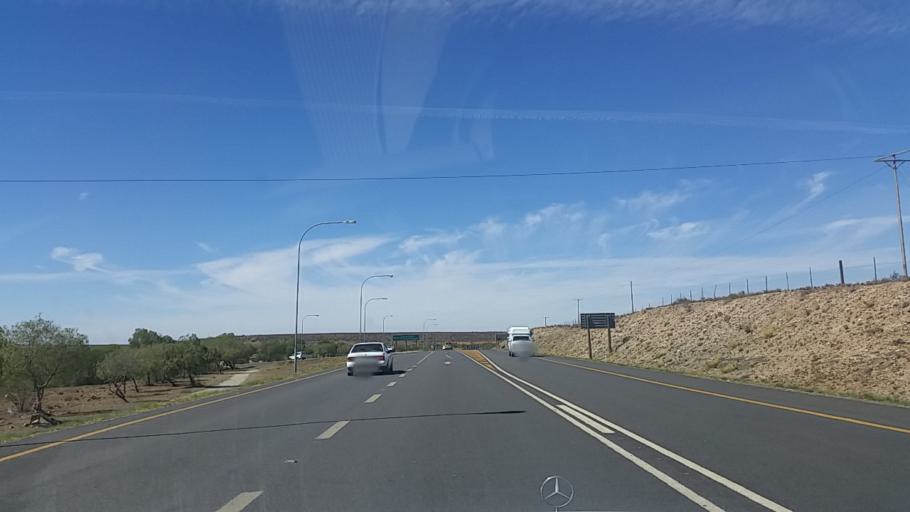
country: ZA
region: Eastern Cape
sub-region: Cacadu District Municipality
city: Graaff-Reinet
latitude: -32.2698
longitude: 24.5450
